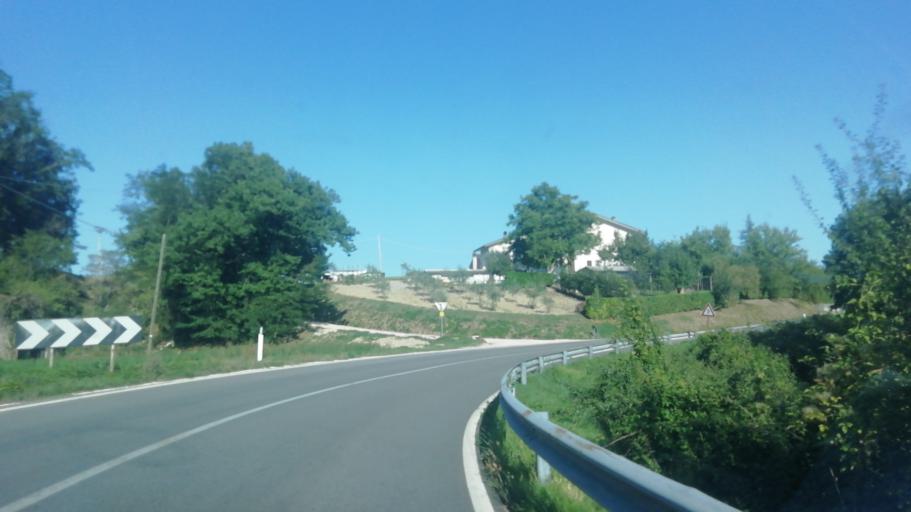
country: IT
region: The Marches
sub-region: Provincia di Pesaro e Urbino
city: Frontone
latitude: 43.5440
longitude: 12.7684
